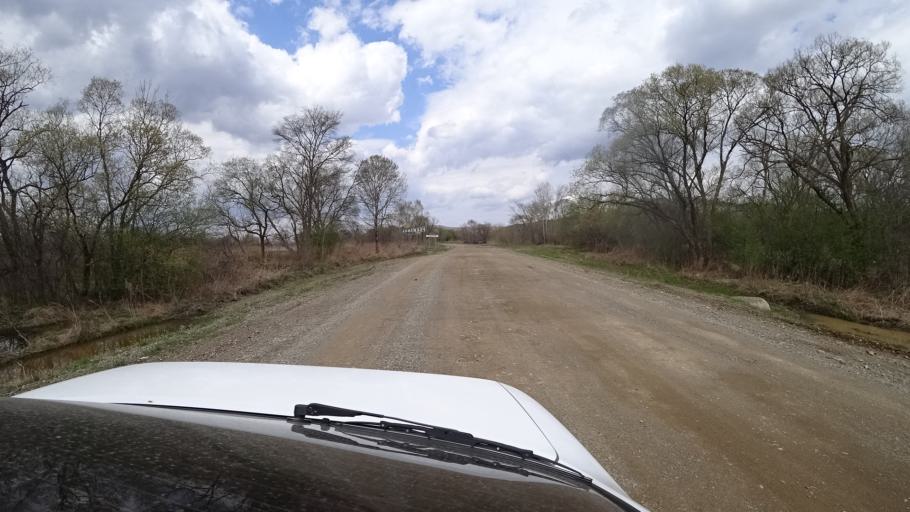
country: RU
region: Primorskiy
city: Novopokrovka
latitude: 45.6120
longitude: 134.2744
